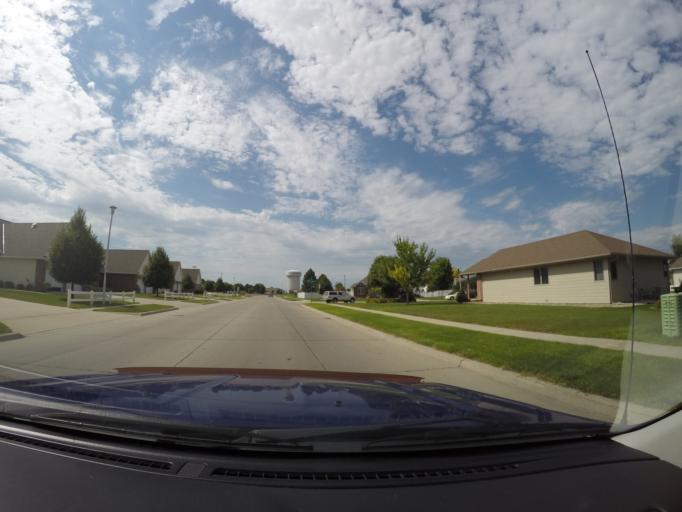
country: US
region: Nebraska
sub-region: Buffalo County
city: Kearney
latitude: 40.7171
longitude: -99.0896
